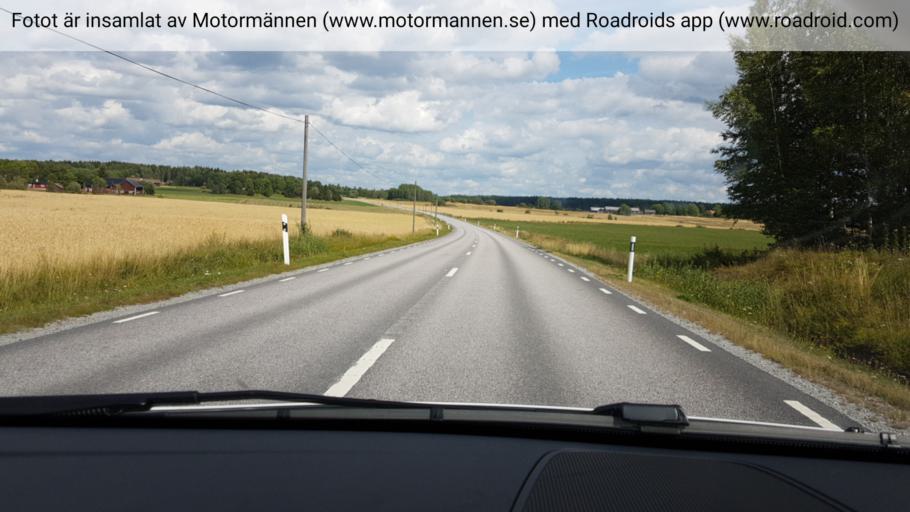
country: SE
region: Stockholm
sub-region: Vallentuna Kommun
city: Vallentuna
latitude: 59.7119
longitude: 18.0524
